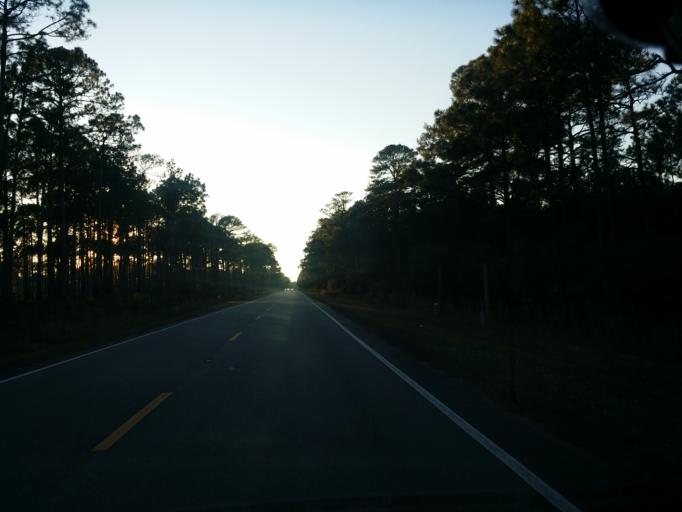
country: US
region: Florida
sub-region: Franklin County
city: Carrabelle
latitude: 29.9214
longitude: -84.4944
